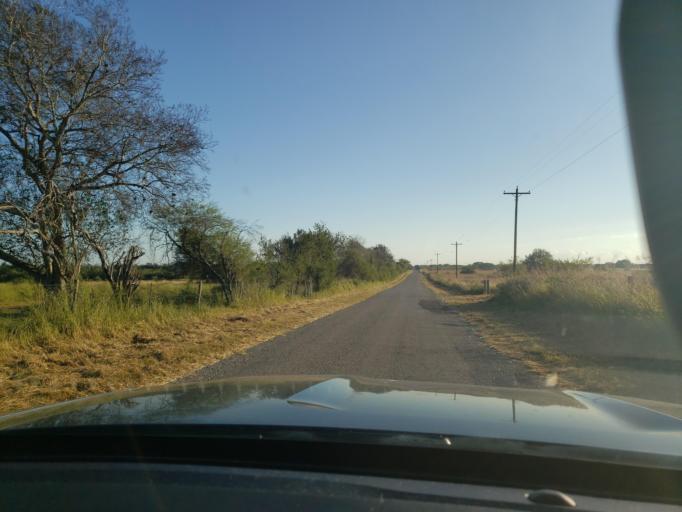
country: US
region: Texas
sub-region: Bee County
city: Beeville
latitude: 28.4178
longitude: -97.7180
